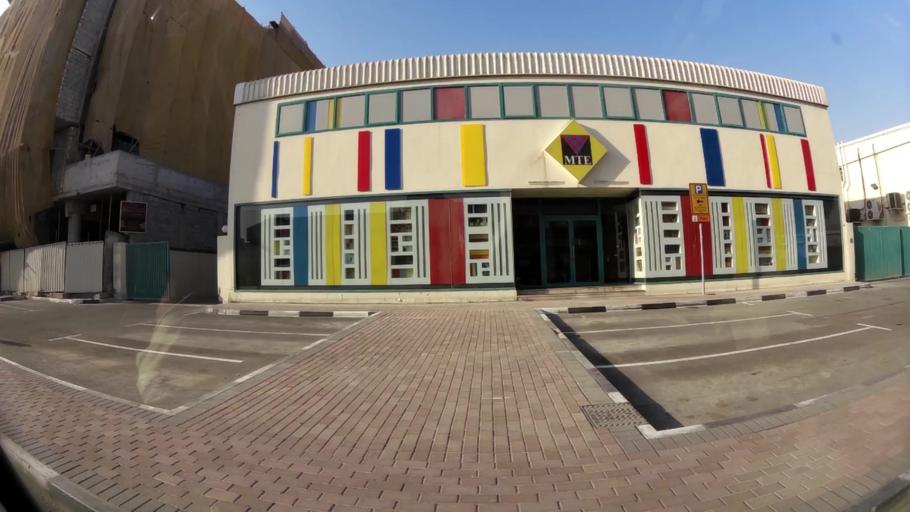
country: AE
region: Ash Shariqah
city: Sharjah
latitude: 25.2516
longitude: 55.3432
